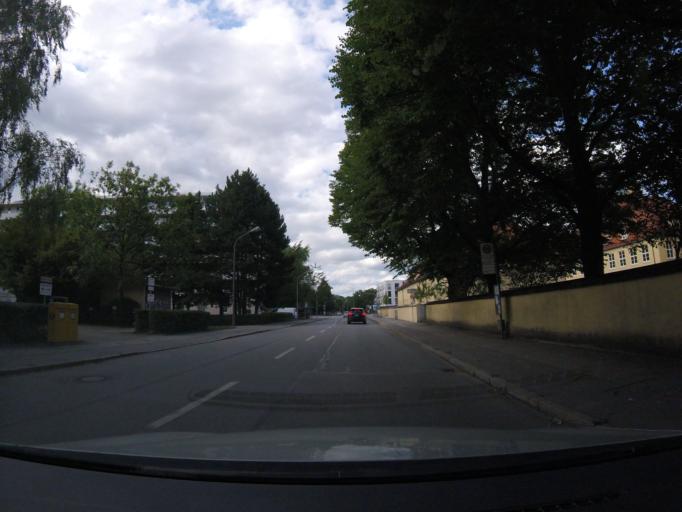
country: DE
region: Bavaria
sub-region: Upper Bavaria
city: Bogenhausen
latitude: 48.1556
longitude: 11.6416
